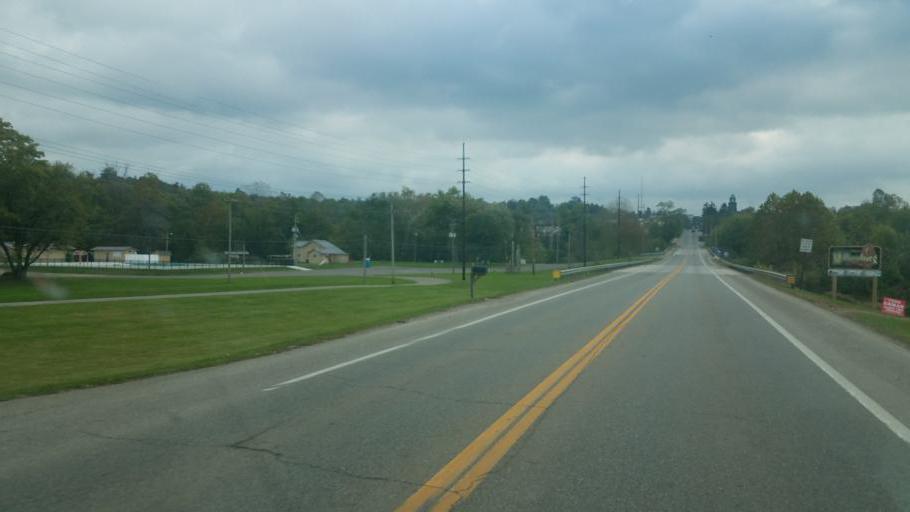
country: US
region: Ohio
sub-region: Holmes County
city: Millersburg
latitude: 40.5544
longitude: -81.9252
